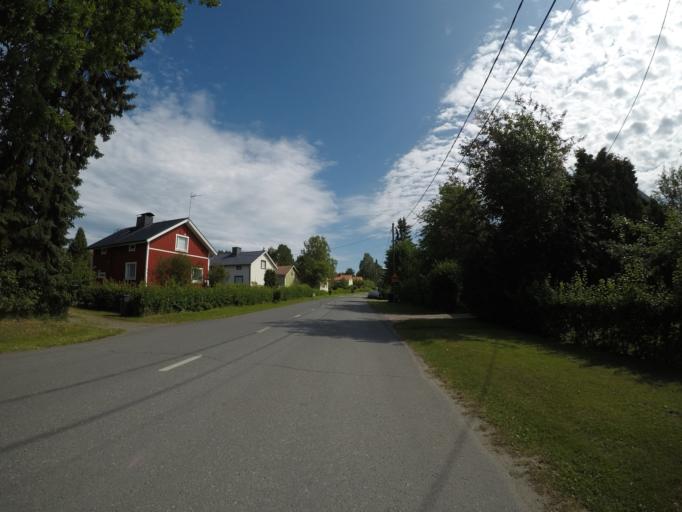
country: FI
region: Haeme
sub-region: Haemeenlinna
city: Haemeenlinna
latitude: 60.9887
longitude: 24.4052
